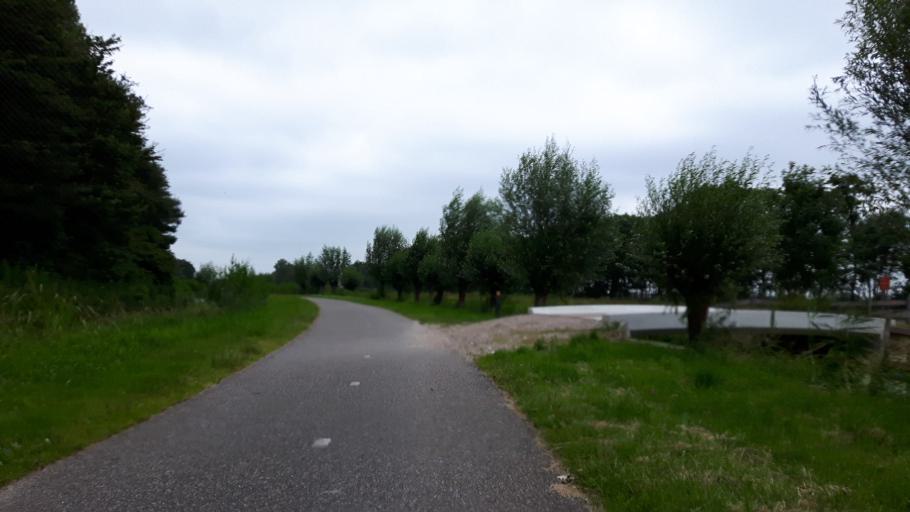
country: NL
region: South Holland
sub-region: Gemeente Gouda
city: Bloemendaal
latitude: 52.0327
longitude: 4.6851
